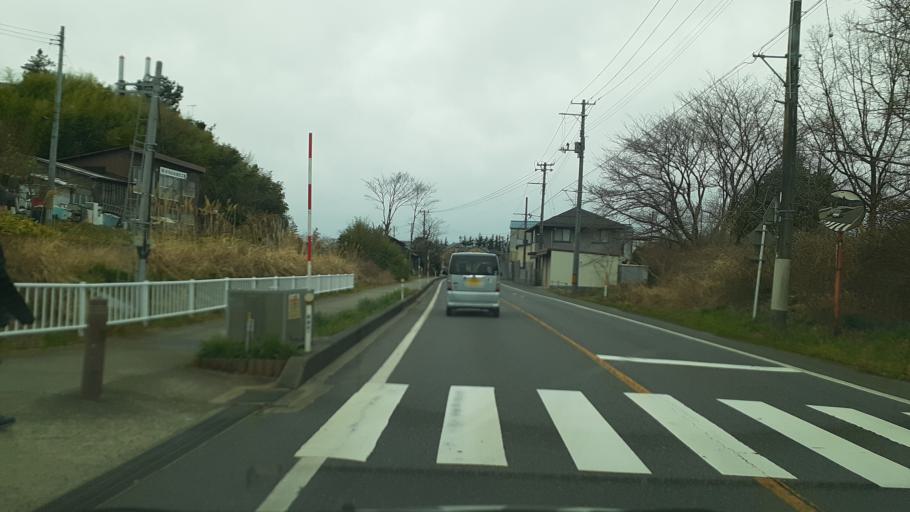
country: JP
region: Niigata
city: Niitsu-honcho
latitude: 37.7922
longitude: 139.1374
